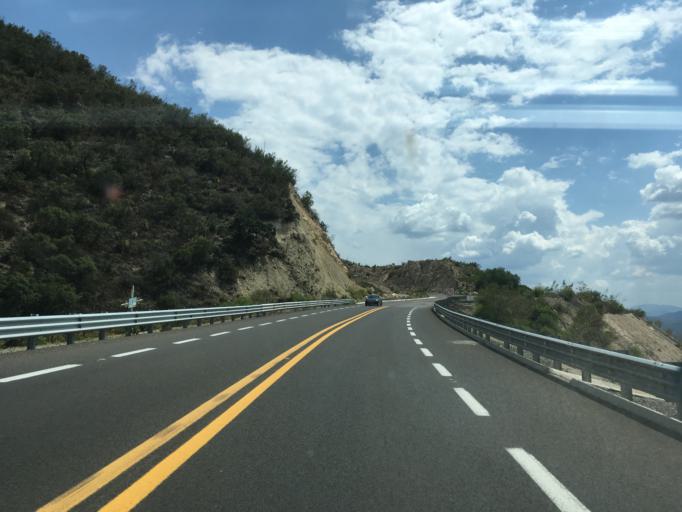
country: MX
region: Puebla
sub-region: San Jose Miahuatlan
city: San Pedro Tetitlan
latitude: 18.0447
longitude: -97.3505
